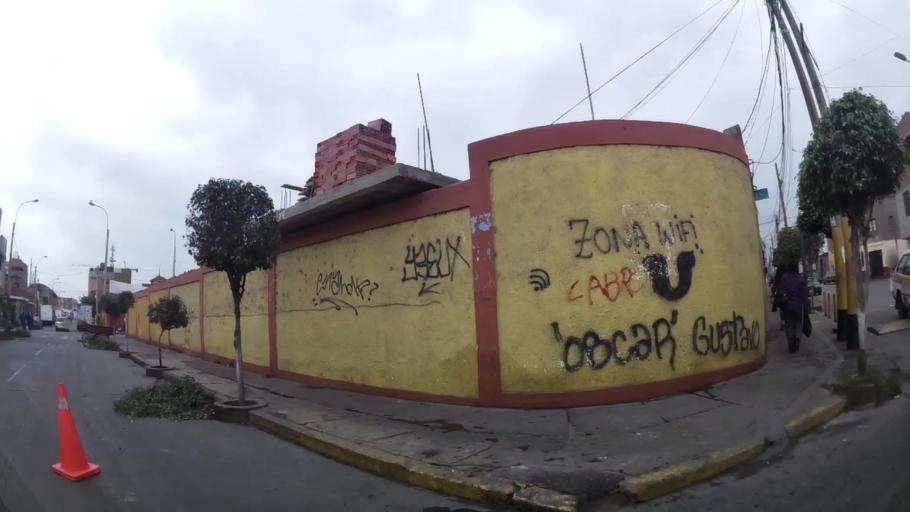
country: PE
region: Lima
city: Lima
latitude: -12.0534
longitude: -77.0537
